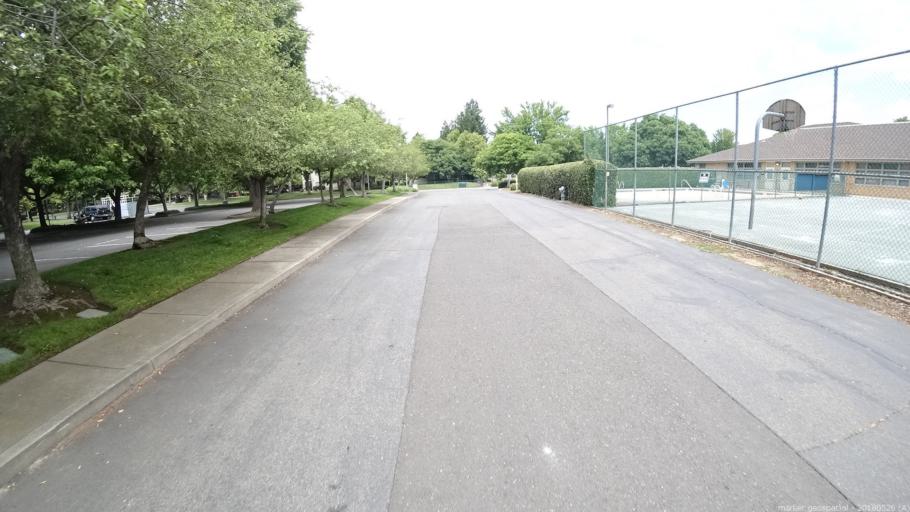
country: US
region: California
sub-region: Sacramento County
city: Sacramento
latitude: 38.6098
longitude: -121.4996
